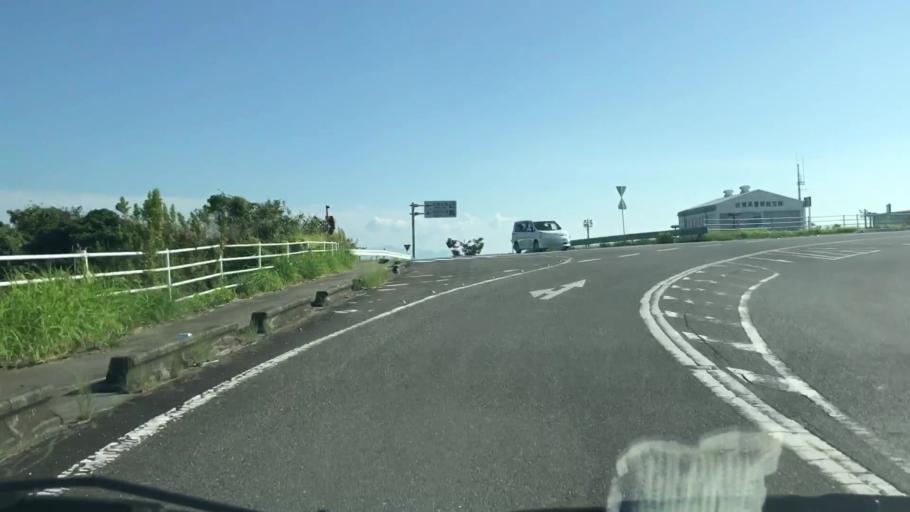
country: JP
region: Saga Prefecture
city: Okawa
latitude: 33.1535
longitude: 130.3076
